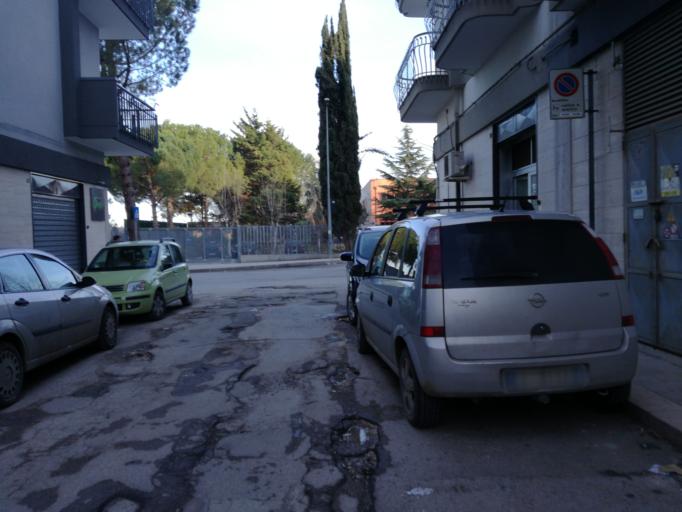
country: IT
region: Apulia
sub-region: Provincia di Bari
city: Corato
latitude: 41.1496
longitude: 16.4174
